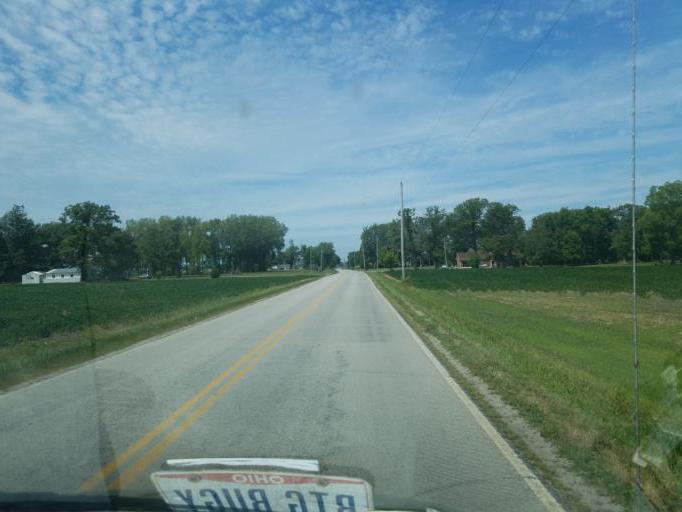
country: US
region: Ohio
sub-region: Madison County
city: West Jefferson
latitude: 39.9846
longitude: -83.2807
